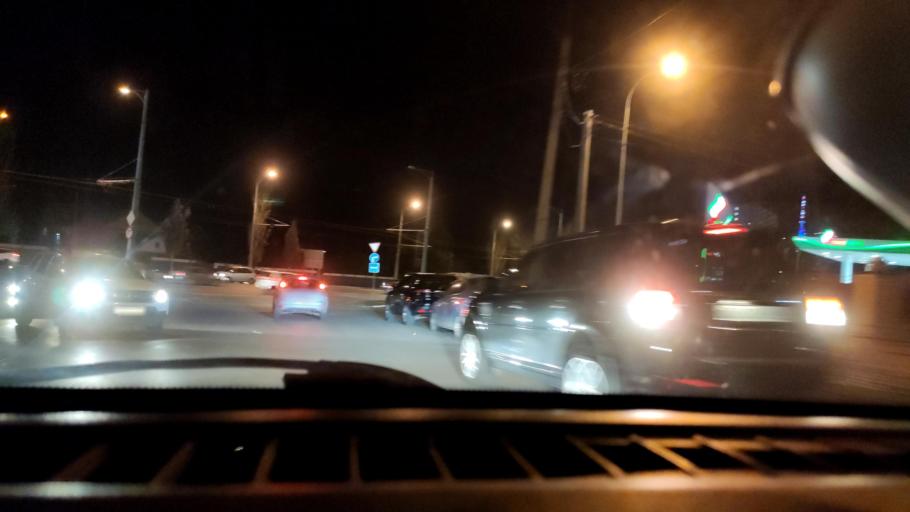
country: RU
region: Samara
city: Samara
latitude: 53.2188
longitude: 50.1890
